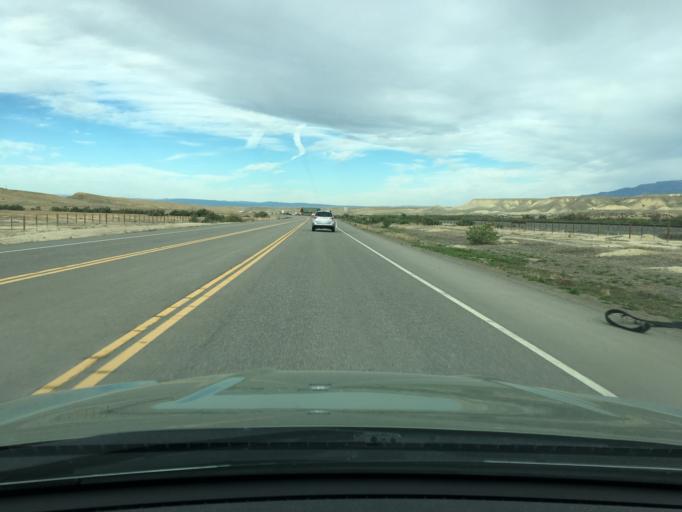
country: US
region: Colorado
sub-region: Delta County
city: Orchard City
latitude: 38.8011
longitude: -107.9054
